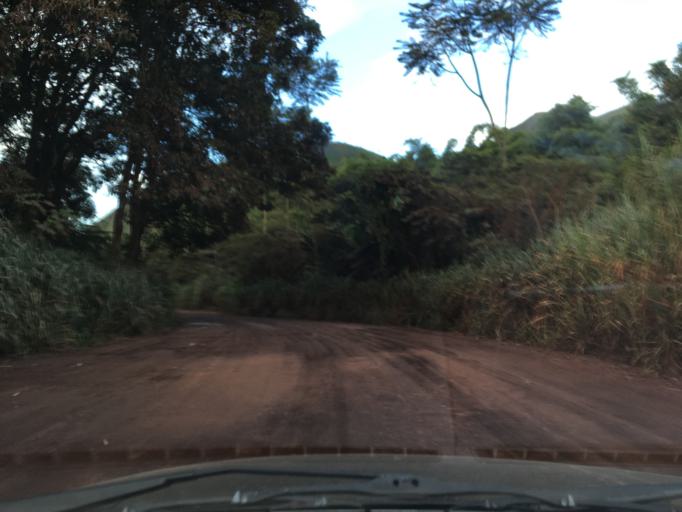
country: BR
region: Minas Gerais
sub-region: Brumadinho
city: Brumadinho
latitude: -20.1064
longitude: -44.2099
